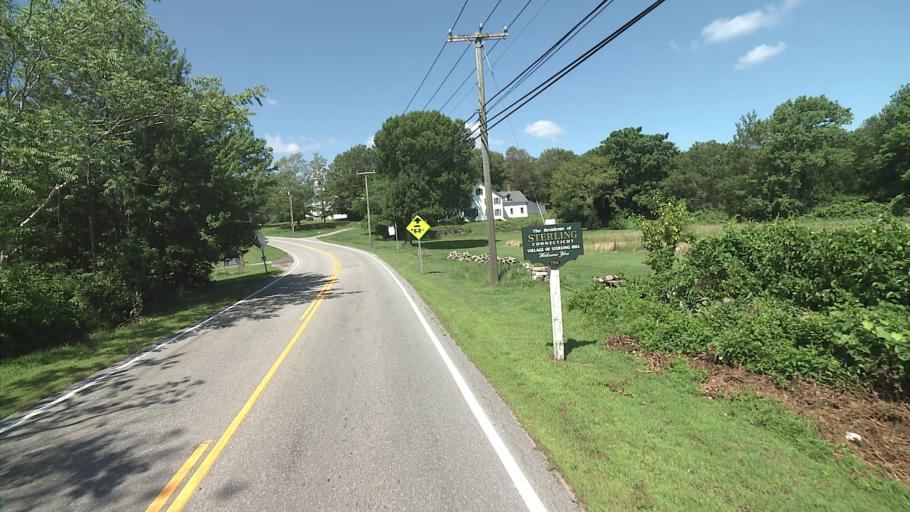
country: US
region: Connecticut
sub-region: Windham County
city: Moosup
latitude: 41.6912
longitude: -71.8446
